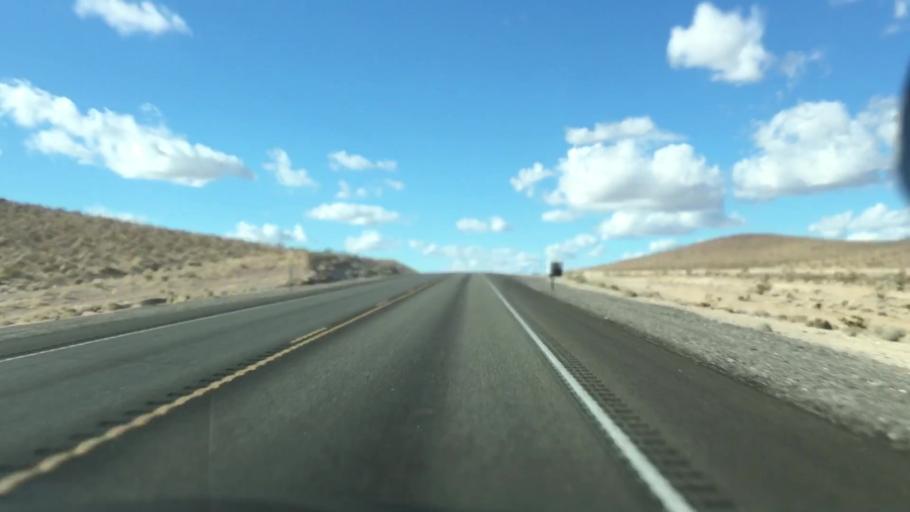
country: US
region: Nevada
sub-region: Nye County
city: Pahrump
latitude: 36.6107
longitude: -116.2708
